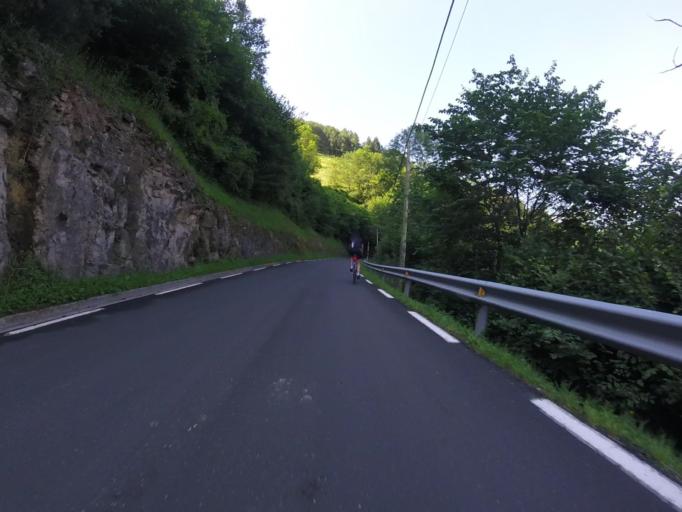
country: ES
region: Basque Country
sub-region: Provincia de Guipuzcoa
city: Larraul
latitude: 43.1783
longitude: -2.0946
